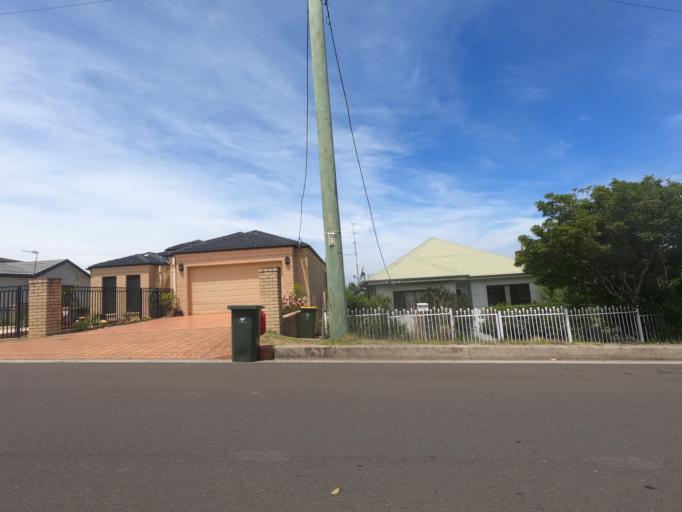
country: AU
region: New South Wales
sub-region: Wollongong
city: Mount Ousley
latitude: -34.3902
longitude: 150.8772
